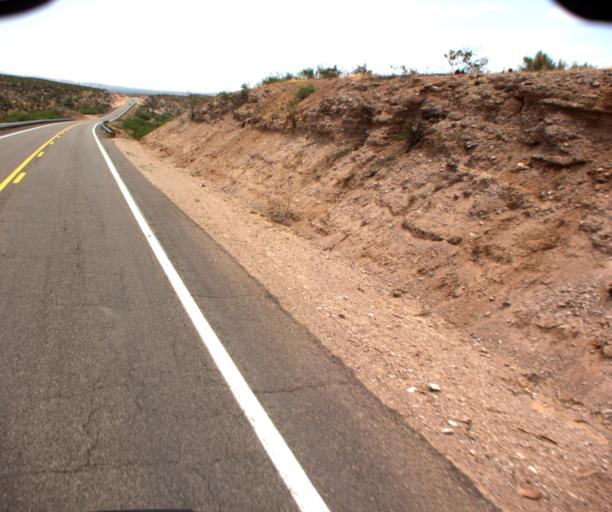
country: US
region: Arizona
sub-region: Graham County
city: Bylas
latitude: 33.2181
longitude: -110.2167
